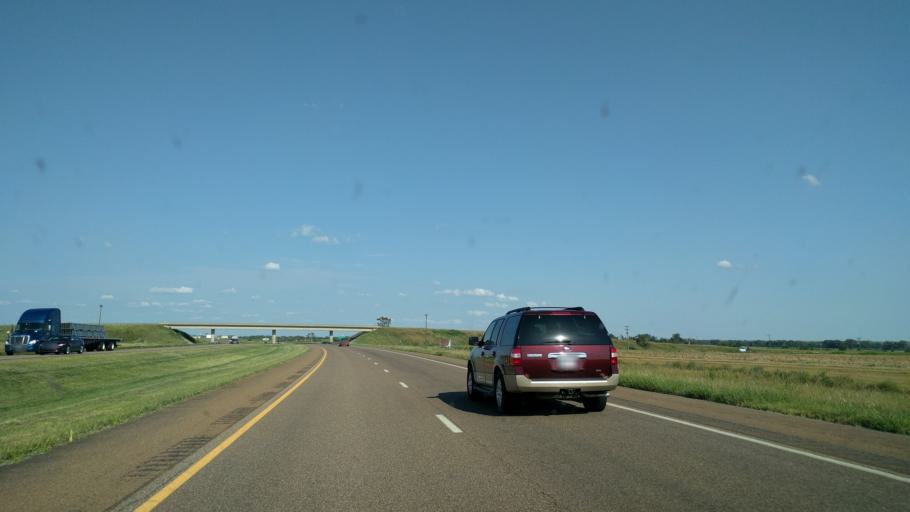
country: US
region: Kansas
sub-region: Ellis County
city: Ellis
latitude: 38.9508
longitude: -99.5979
